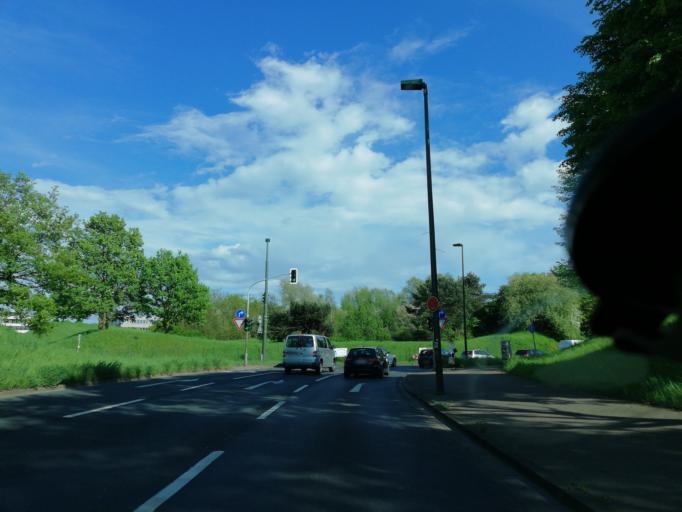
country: DE
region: North Rhine-Westphalia
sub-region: Regierungsbezirk Dusseldorf
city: Dusseldorf
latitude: 51.2000
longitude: 6.7705
